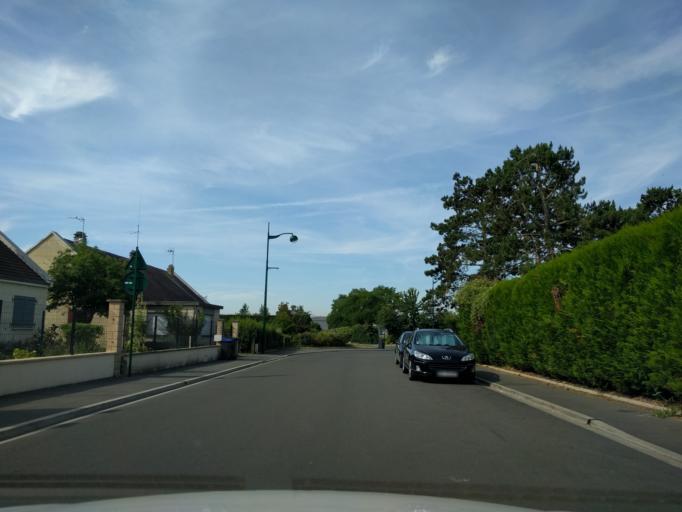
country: FR
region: Picardie
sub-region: Departement de l'Oise
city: Tille
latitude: 49.4609
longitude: 2.1091
